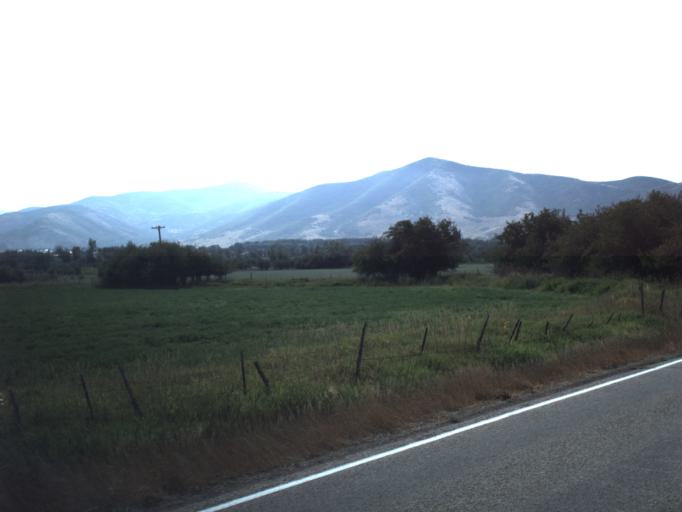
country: US
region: Utah
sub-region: Wasatch County
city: Midway
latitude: 40.4894
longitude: -111.4720
